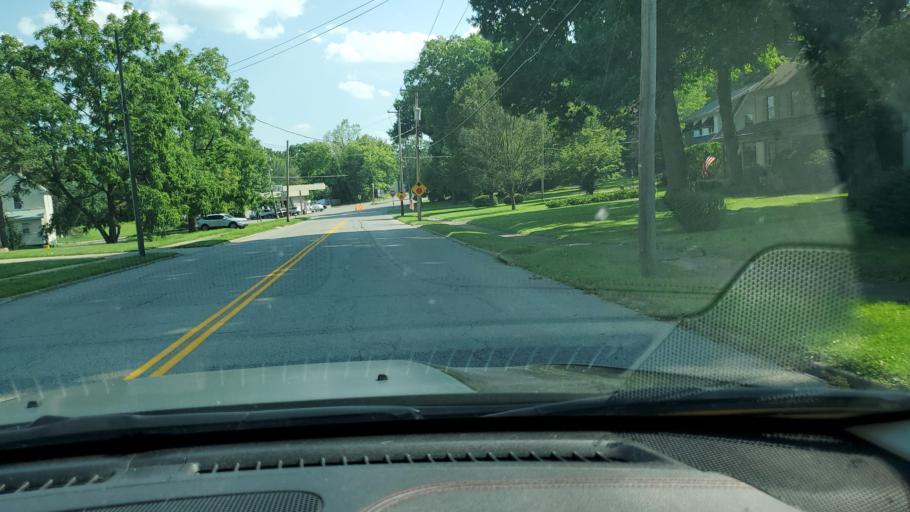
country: US
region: Ohio
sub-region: Mahoning County
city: Struthers
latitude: 41.0388
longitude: -80.6035
